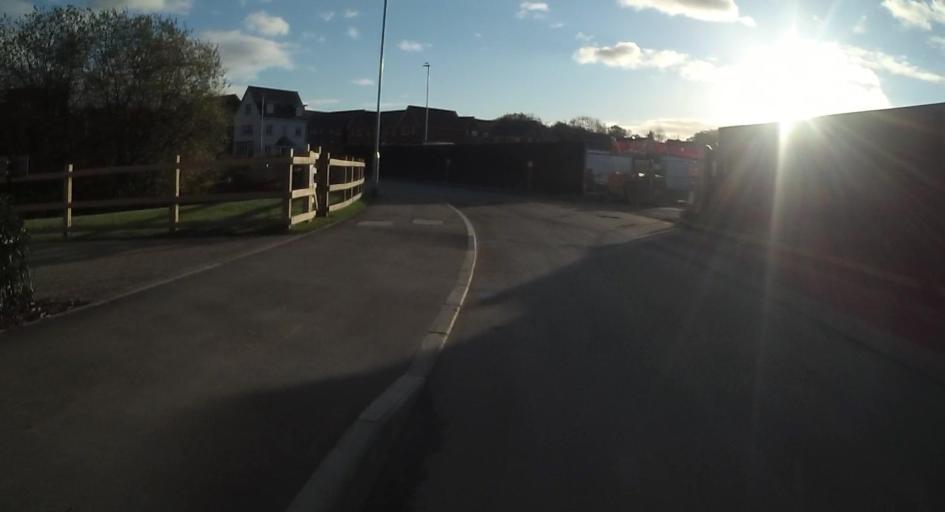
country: GB
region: England
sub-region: Bracknell Forest
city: Binfield
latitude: 51.4259
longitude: -0.7778
